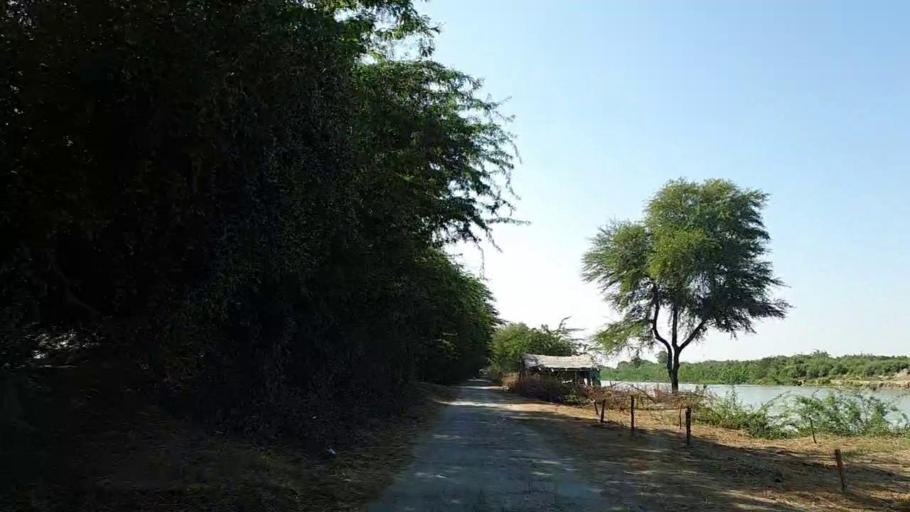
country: PK
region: Sindh
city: Chuhar Jamali
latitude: 24.5735
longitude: 68.0443
